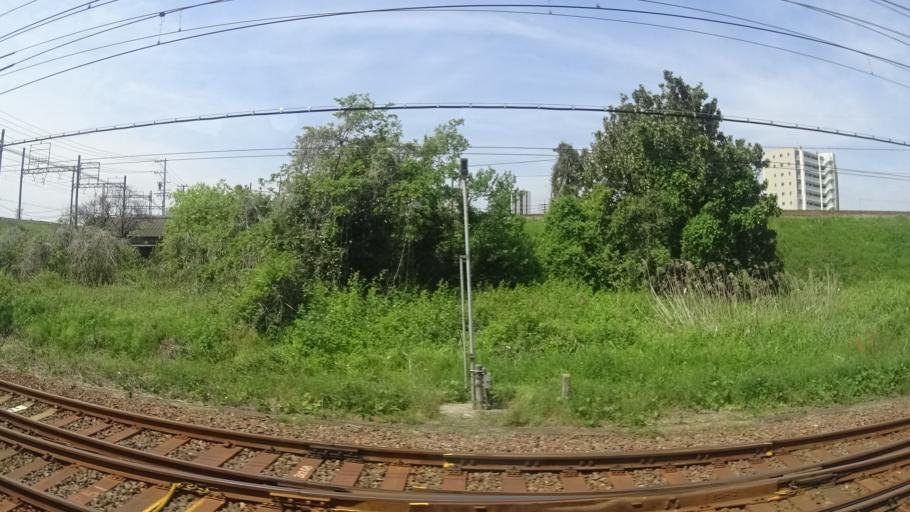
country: JP
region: Mie
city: Yokkaichi
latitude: 35.0108
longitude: 136.6517
